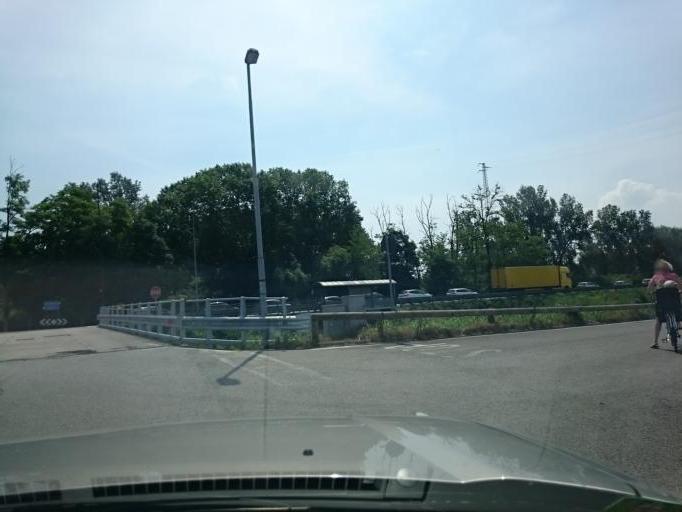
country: IT
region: Veneto
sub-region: Provincia di Padova
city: Codevigo
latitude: 45.2900
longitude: 12.1298
